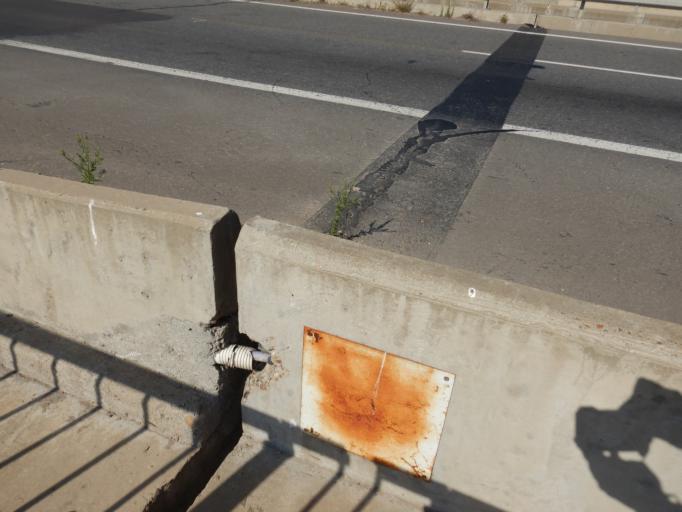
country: AR
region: Entre Rios
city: Parana
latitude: -31.6692
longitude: -60.5817
